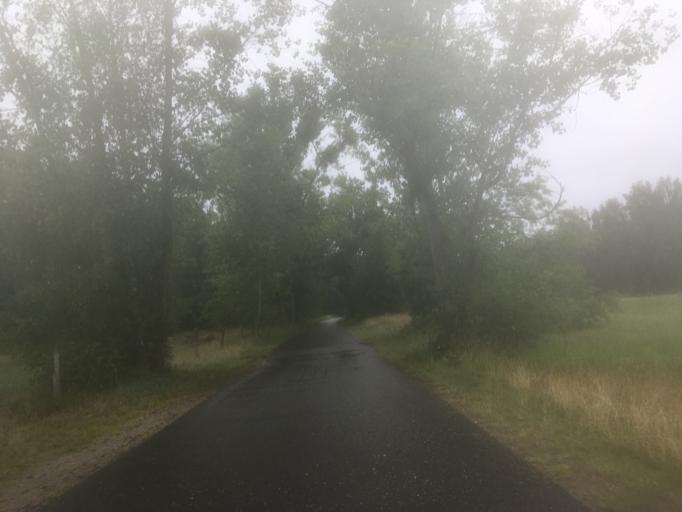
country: DE
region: Brandenburg
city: Zehdenick
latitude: 53.0171
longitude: 13.3099
